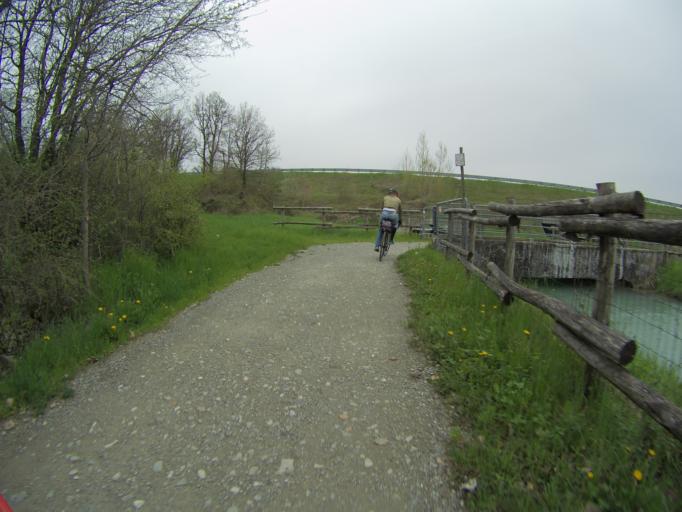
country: IT
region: Emilia-Romagna
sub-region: Provincia di Reggio Emilia
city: Ciano d'Enza
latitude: 44.6163
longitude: 10.4129
